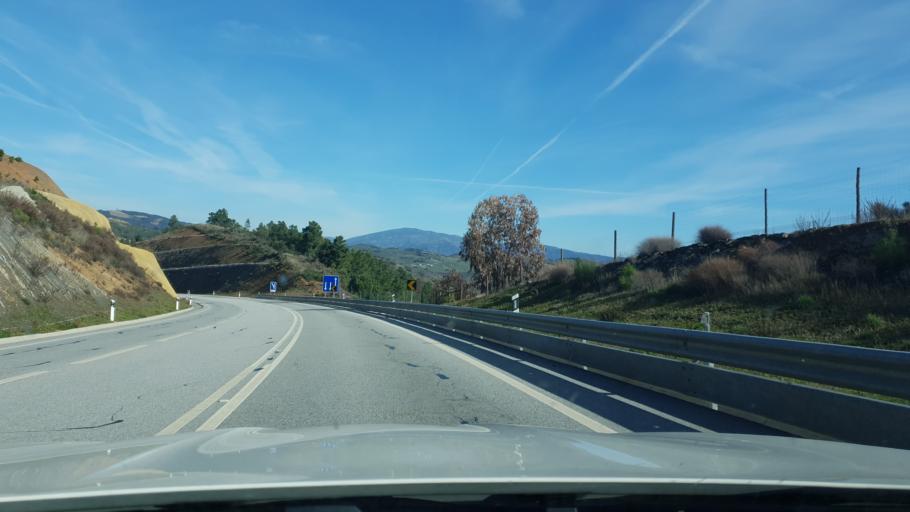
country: PT
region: Braganca
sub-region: Braganca Municipality
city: Vila Flor
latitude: 41.3100
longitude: -7.1251
